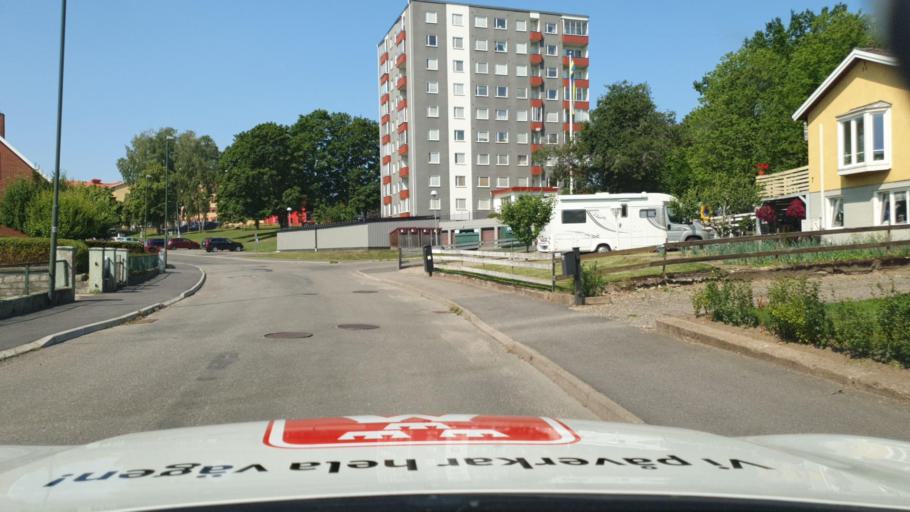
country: SE
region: Vaestra Goetaland
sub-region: Skovde Kommun
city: Skoevde
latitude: 58.3903
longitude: 13.8653
